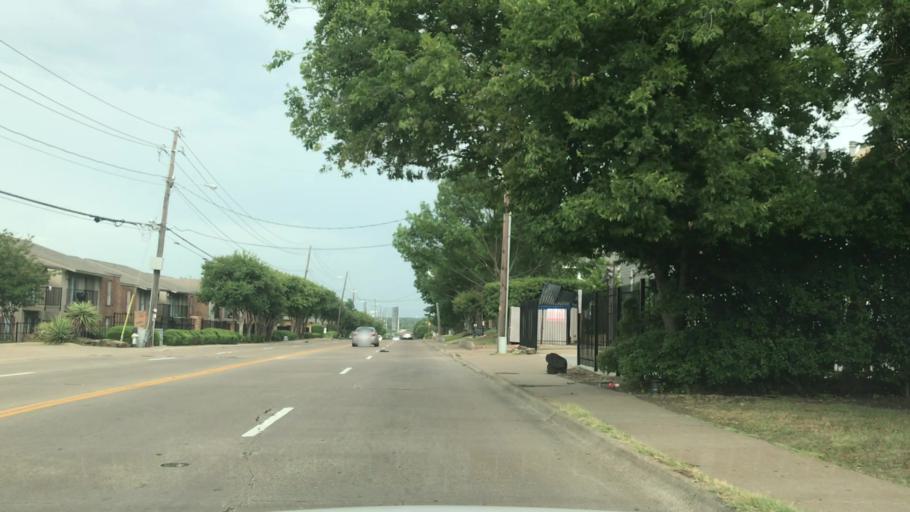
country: US
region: Texas
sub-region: Dallas County
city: University Park
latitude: 32.8709
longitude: -96.7584
